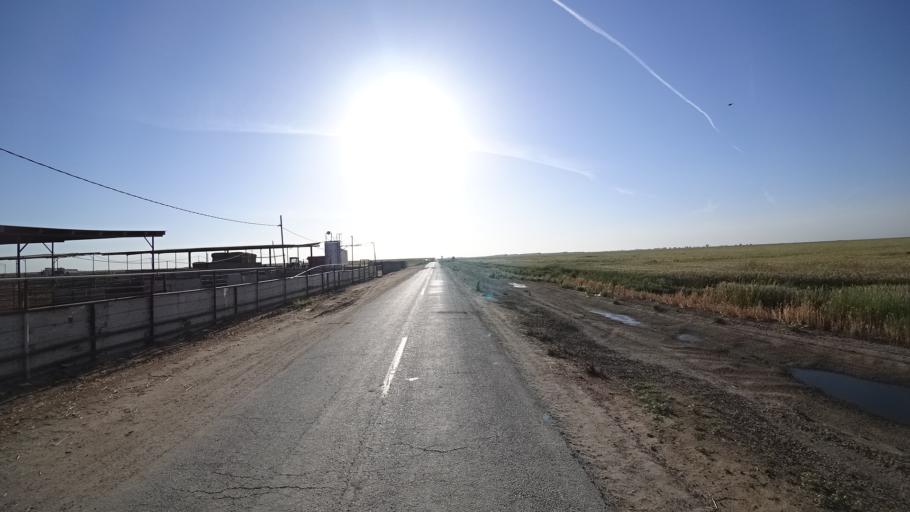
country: US
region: California
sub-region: Kings County
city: Stratford
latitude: 36.1602
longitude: -119.7651
